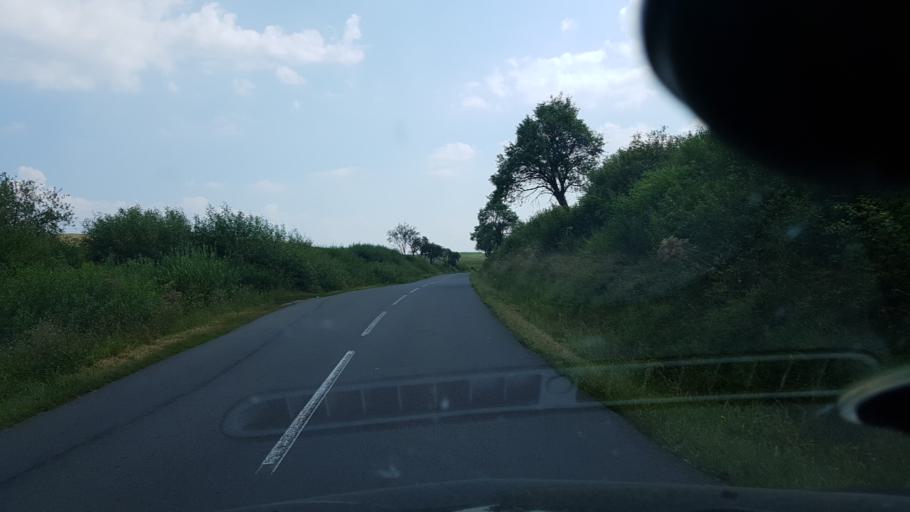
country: SK
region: Banskobystricky
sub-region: Okres Banska Bystrica
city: Zvolen
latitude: 48.5963
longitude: 19.2262
